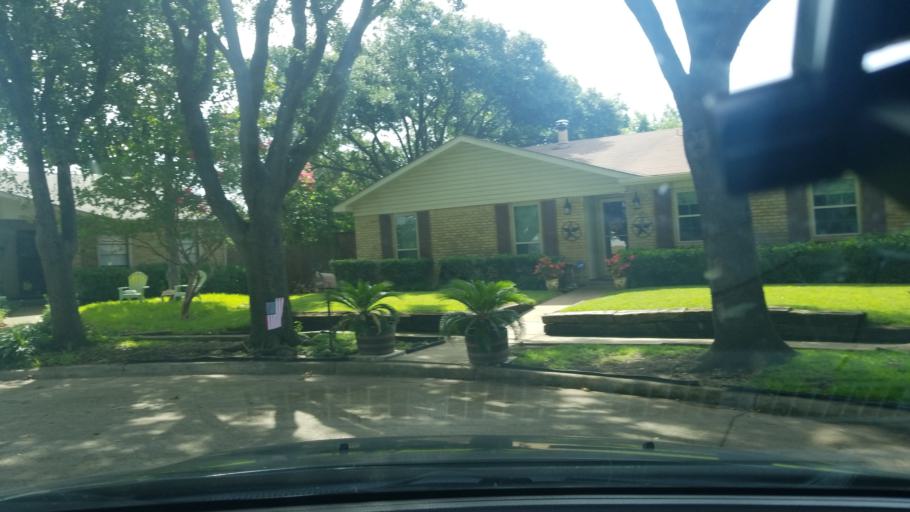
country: US
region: Texas
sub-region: Dallas County
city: Highland Park
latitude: 32.8047
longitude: -96.6944
